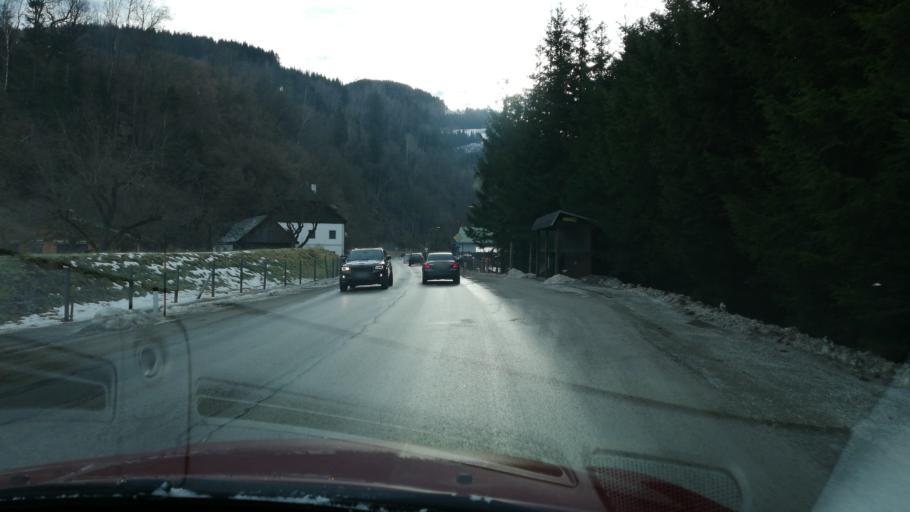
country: AT
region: Styria
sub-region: Politischer Bezirk Liezen
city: Irdning
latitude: 47.4976
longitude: 14.1015
